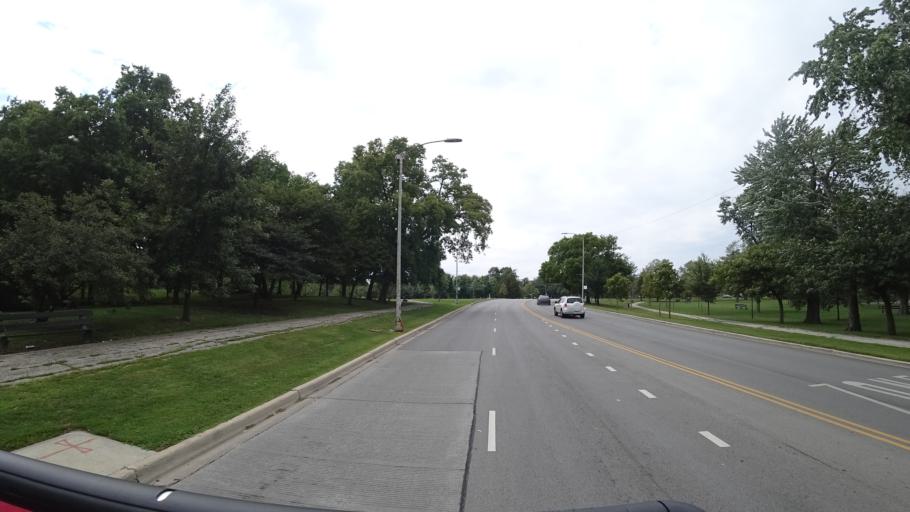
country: US
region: Illinois
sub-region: Cook County
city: Oak Park
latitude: 41.8765
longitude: -87.7651
